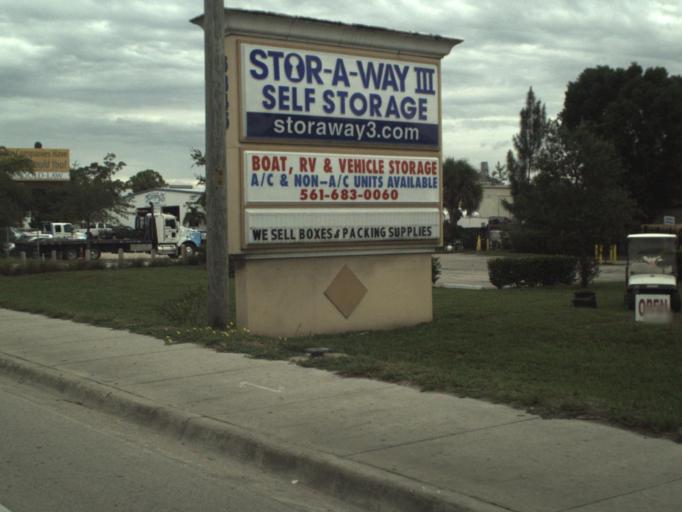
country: US
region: Florida
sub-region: Palm Beach County
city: Lake Belvedere Estates
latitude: 26.6791
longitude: -80.1551
